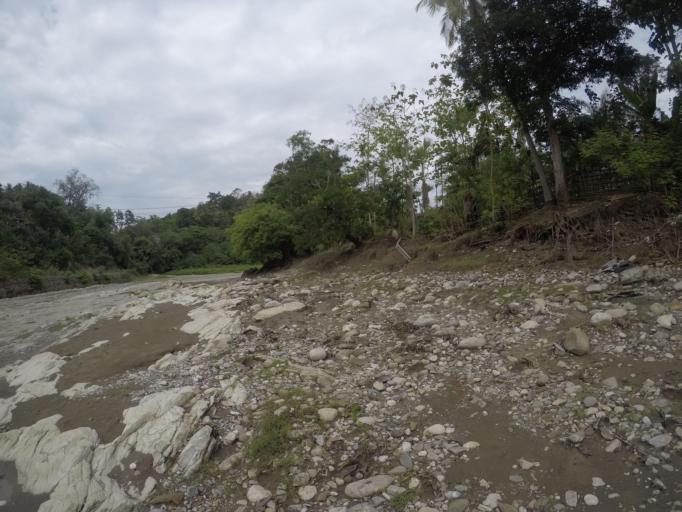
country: TL
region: Viqueque
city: Viqueque
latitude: -8.8651
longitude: 126.3639
